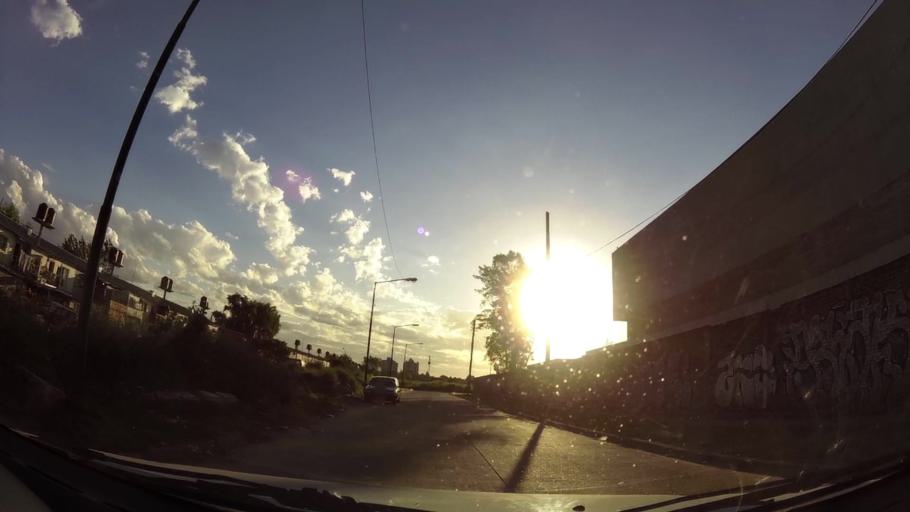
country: AR
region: Buenos Aires
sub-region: Partido de San Isidro
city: San Isidro
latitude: -34.4656
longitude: -58.5512
